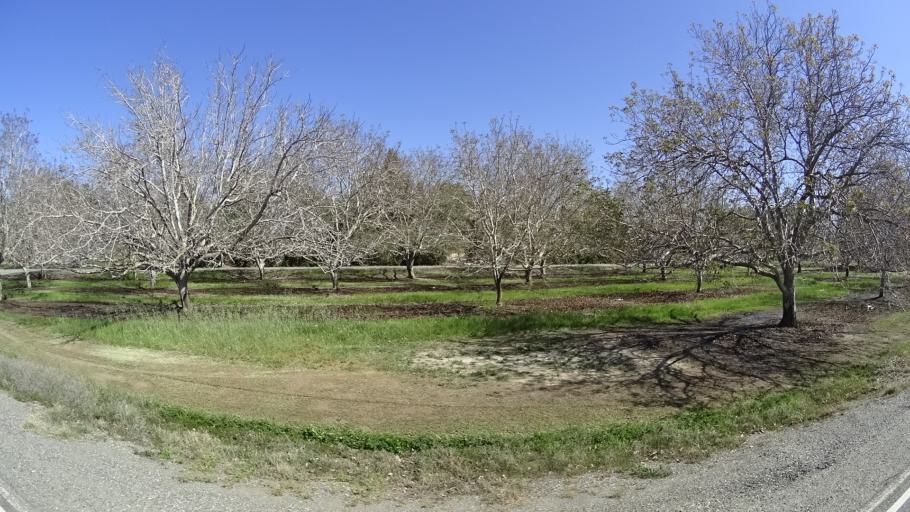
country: US
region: California
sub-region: Glenn County
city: Hamilton City
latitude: 39.7084
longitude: -122.0052
